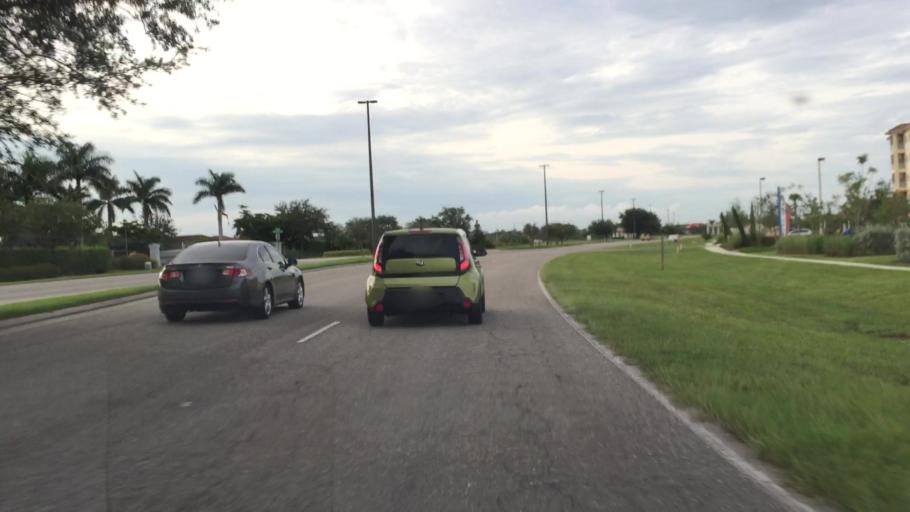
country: US
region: Florida
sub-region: Lee County
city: Fort Myers
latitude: 26.6274
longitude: -81.7938
